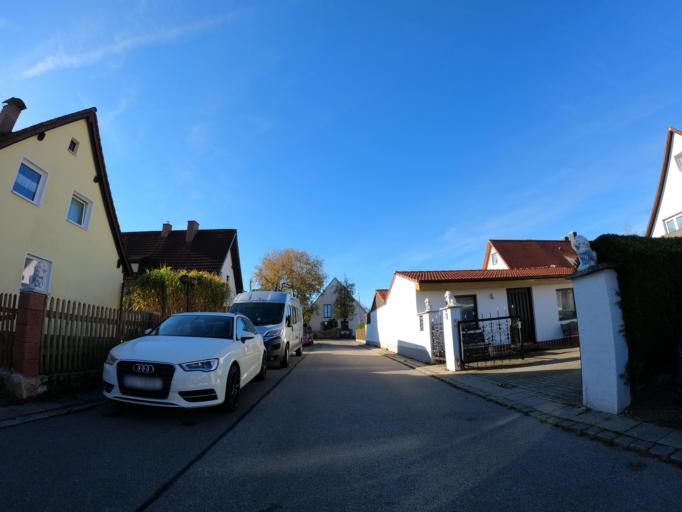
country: DE
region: Bavaria
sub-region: Upper Bavaria
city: Oberhaching
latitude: 48.0305
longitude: 11.6040
